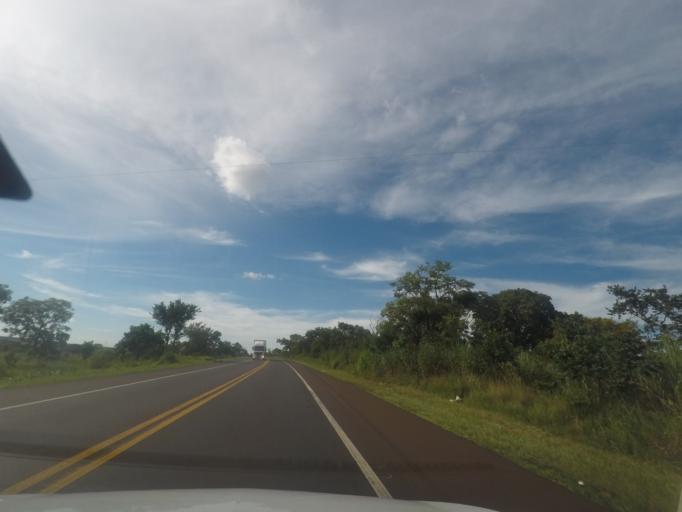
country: BR
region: Minas Gerais
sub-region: Monte Alegre De Minas
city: Monte Alegre de Minas
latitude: -18.9668
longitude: -49.0256
